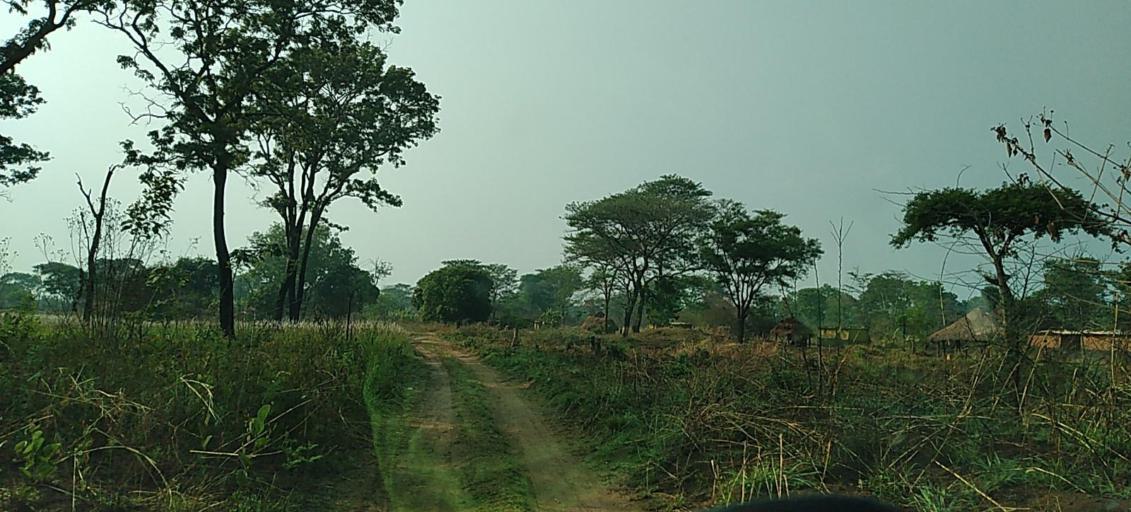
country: ZM
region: North-Western
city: Solwezi
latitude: -12.3835
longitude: 26.5661
